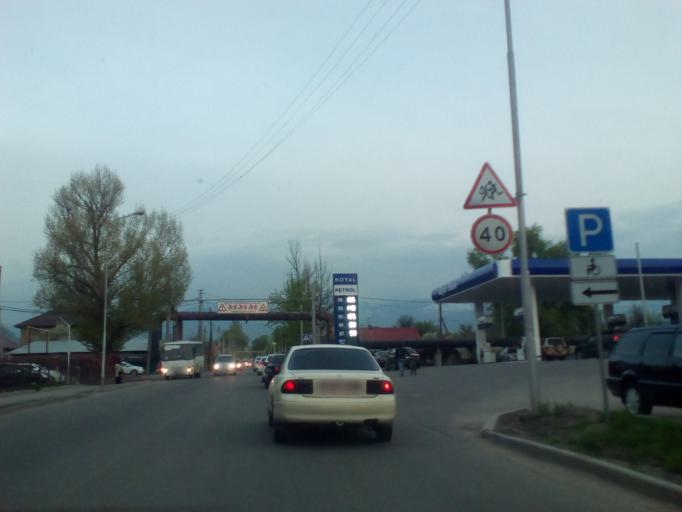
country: KZ
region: Almaty Qalasy
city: Almaty
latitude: 43.2341
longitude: 76.8253
